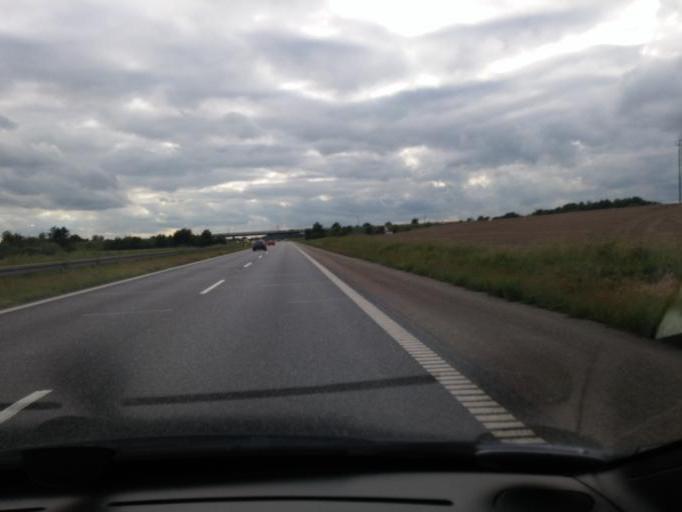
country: DK
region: Zealand
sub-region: Koge Kommune
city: Ejby
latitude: 55.4797
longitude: 12.1182
